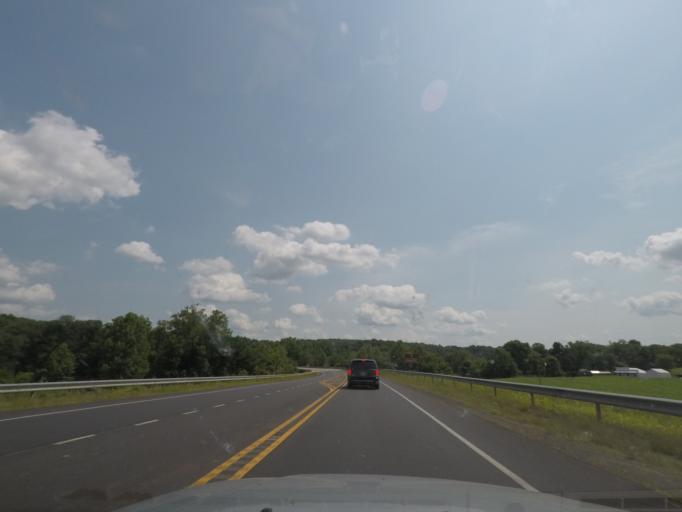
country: US
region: Virginia
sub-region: Orange County
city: Orange
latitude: 38.2829
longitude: -78.1397
